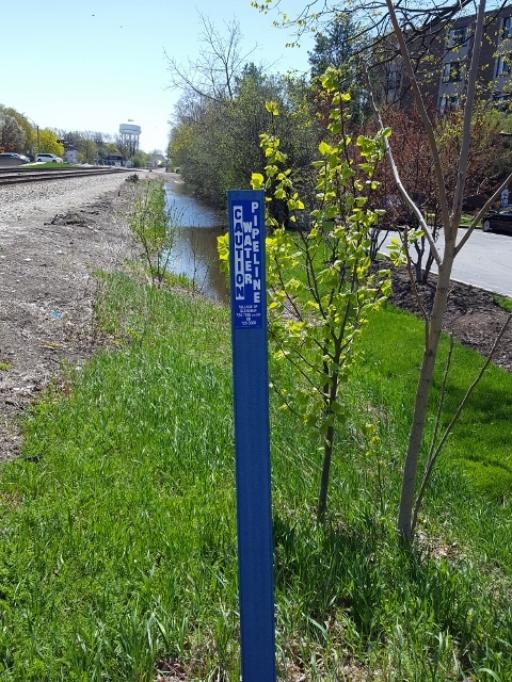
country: US
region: Illinois
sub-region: Cook County
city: Glenview
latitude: 42.0727
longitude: -87.8048
